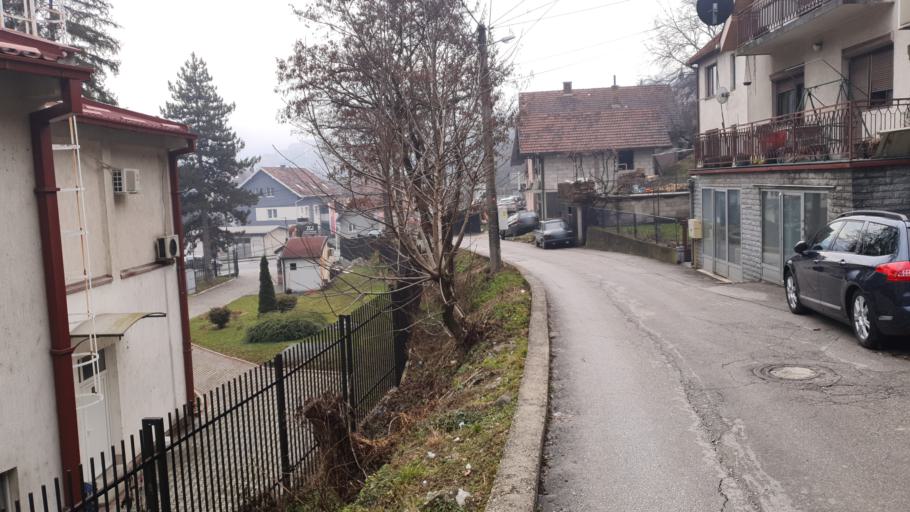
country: RS
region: Central Serbia
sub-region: Zlatiborski Okrug
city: Uzice
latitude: 43.8641
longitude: 19.8243
